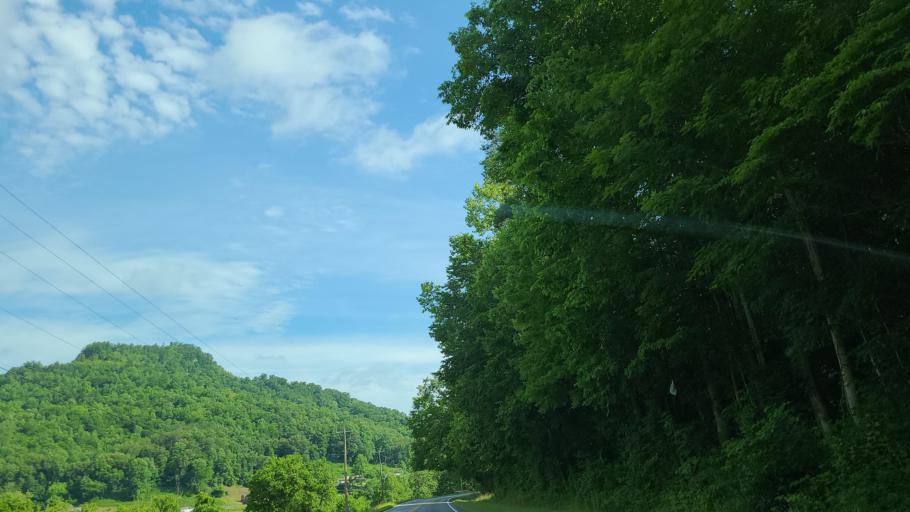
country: US
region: Kentucky
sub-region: Bell County
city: Pineville
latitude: 36.7761
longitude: -83.7710
